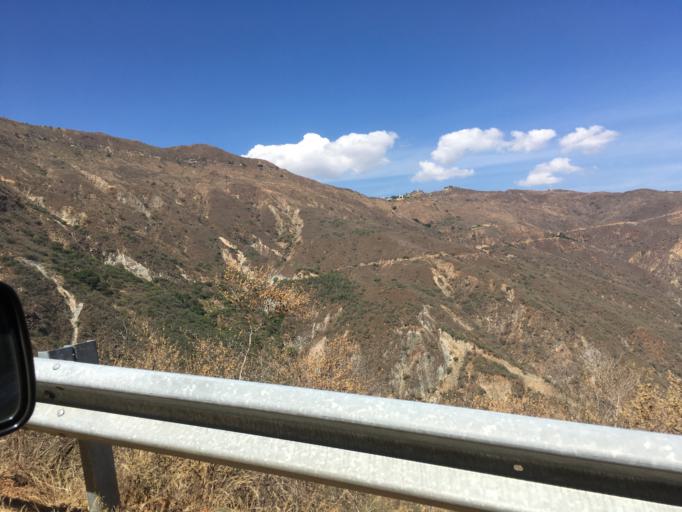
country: CO
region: Santander
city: Aratoca
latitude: 6.7714
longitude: -72.9867
